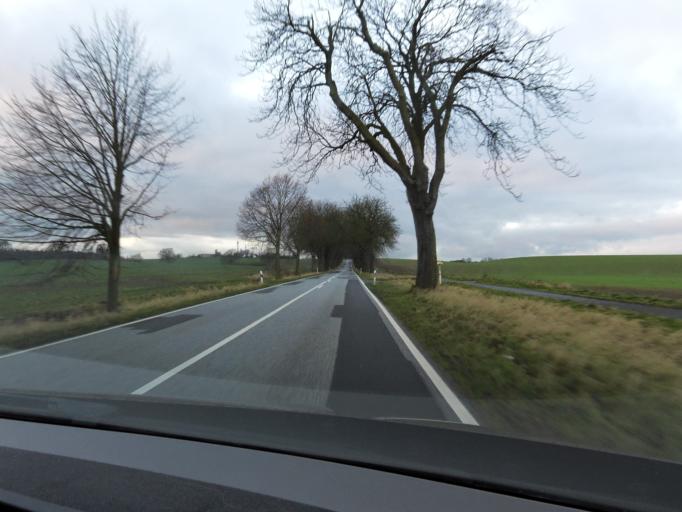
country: DE
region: Mecklenburg-Vorpommern
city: Roggendorf
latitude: 53.6953
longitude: 11.0055
